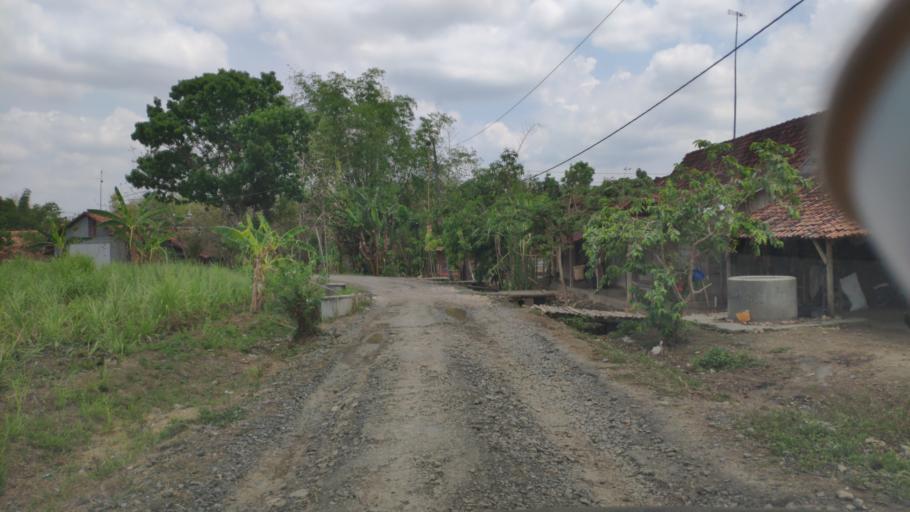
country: ID
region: Central Java
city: Gumiring
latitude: -7.0425
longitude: 111.3919
